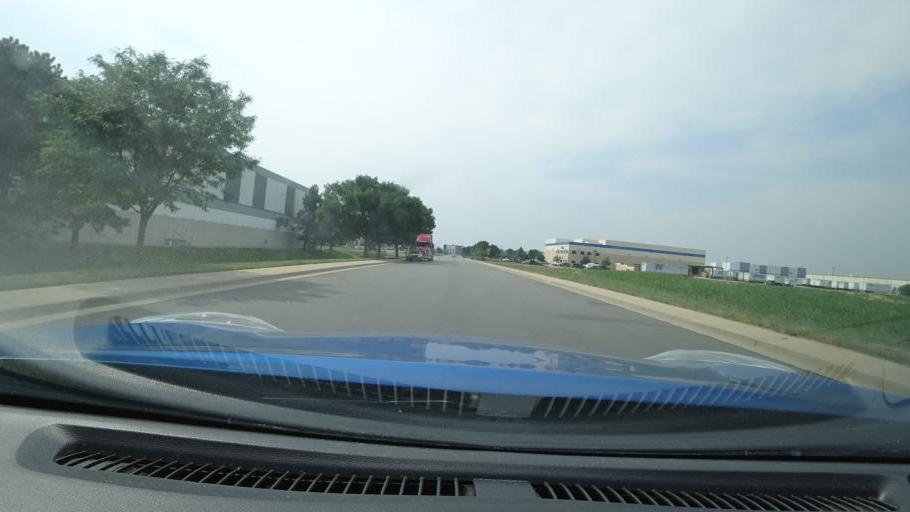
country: US
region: Colorado
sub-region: Adams County
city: Aurora
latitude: 39.7625
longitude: -104.7392
